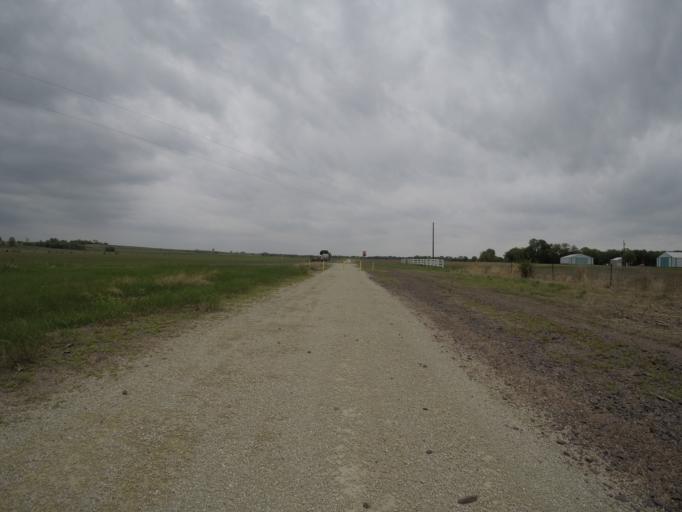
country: US
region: Nebraska
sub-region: Gage County
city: Wymore
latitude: 40.0878
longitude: -96.5959
